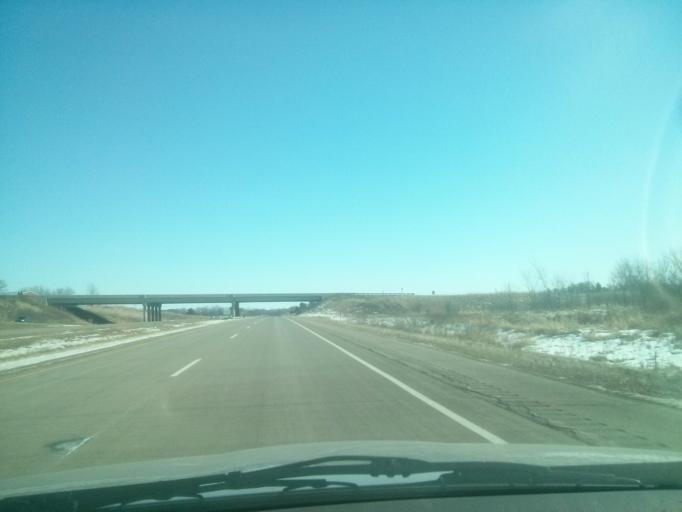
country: US
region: Wisconsin
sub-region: Saint Croix County
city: Somerset
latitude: 45.1198
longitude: -92.6575
